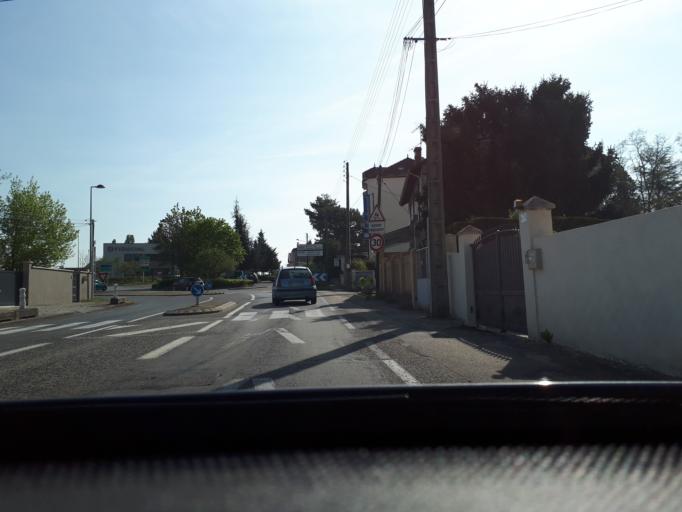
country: FR
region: Rhone-Alpes
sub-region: Departement de l'Isere
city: Bourgoin-Jallieu
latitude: 45.5854
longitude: 5.2593
